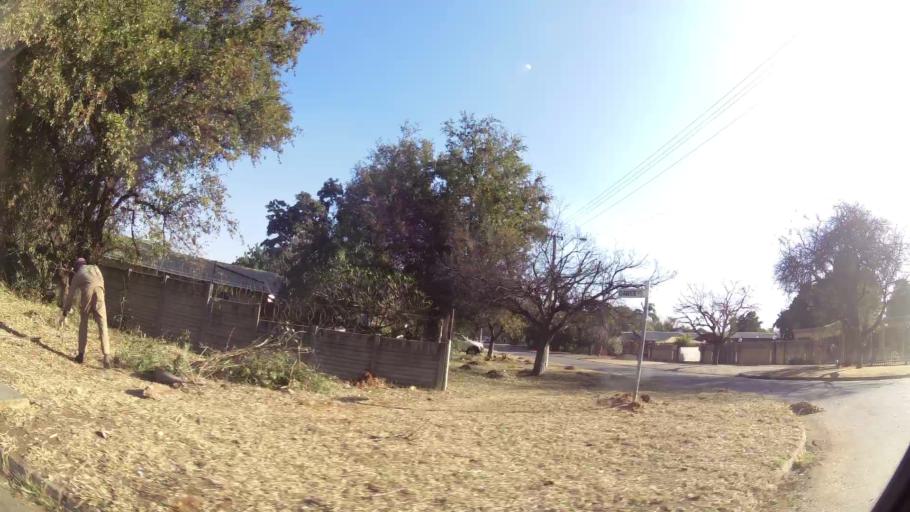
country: ZA
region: North-West
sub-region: Bojanala Platinum District Municipality
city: Rustenburg
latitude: -25.6529
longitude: 27.2539
